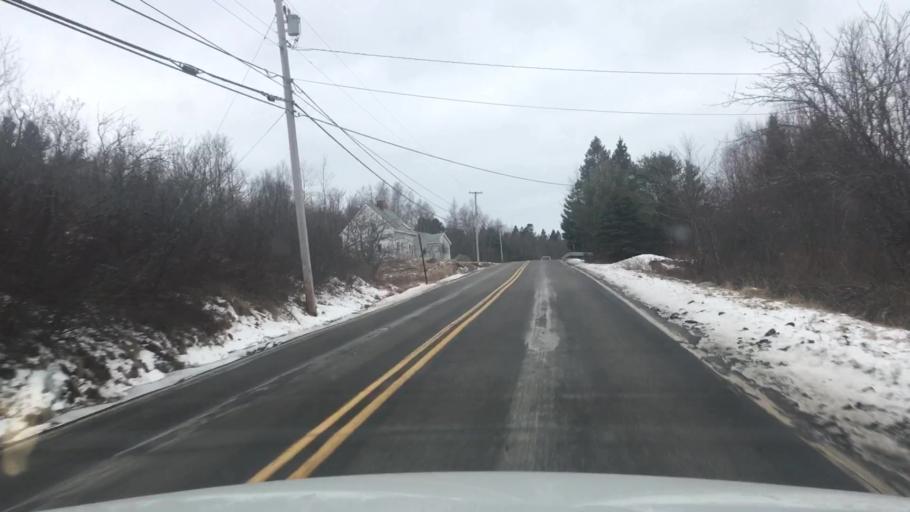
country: US
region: Maine
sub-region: Washington County
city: East Machias
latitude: 44.7257
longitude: -67.3872
